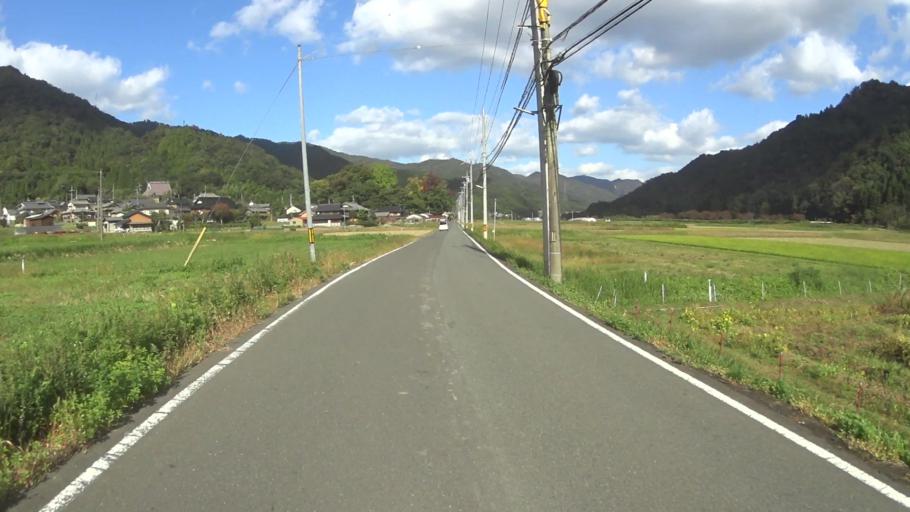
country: JP
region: Kyoto
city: Maizuru
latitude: 35.5191
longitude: 135.4032
